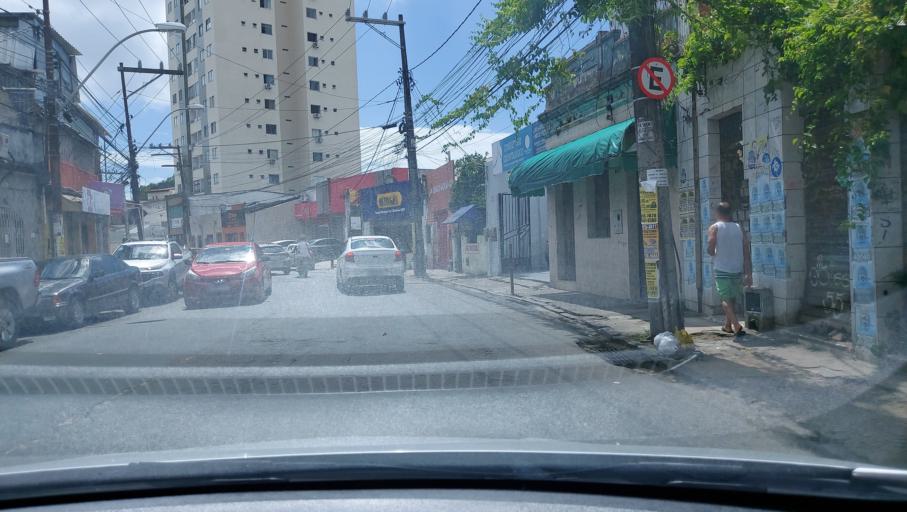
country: BR
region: Bahia
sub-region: Salvador
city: Salvador
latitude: -12.9789
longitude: -38.4987
